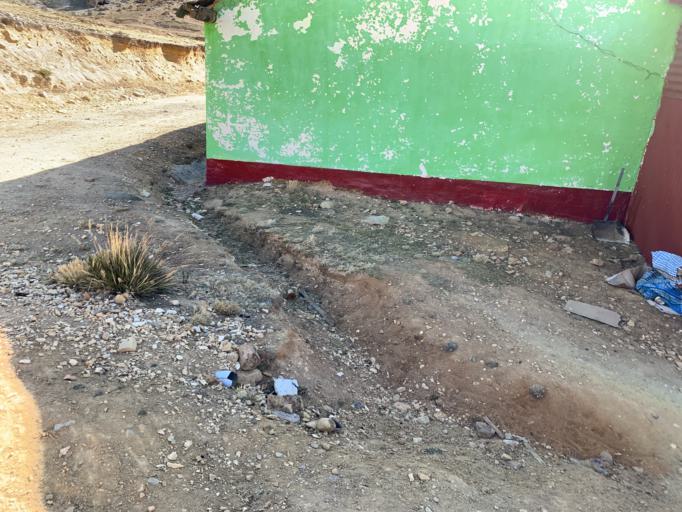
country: PE
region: Huancavelica
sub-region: Provincia de Huancavelica
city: Acobambilla
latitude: -12.6378
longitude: -75.5332
